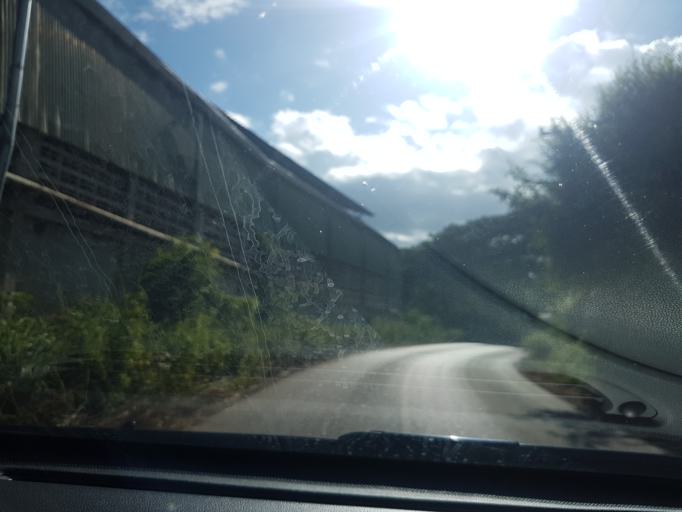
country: TH
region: Lampang
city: Ko Kha
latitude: 18.2312
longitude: 99.4289
